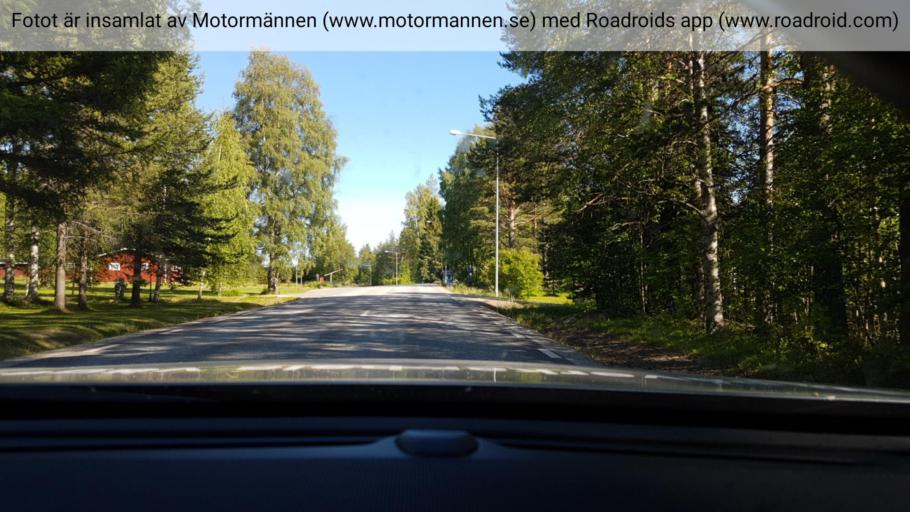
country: SE
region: Vaesterbotten
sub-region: Lycksele Kommun
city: Lycksele
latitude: 64.6360
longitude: 18.5373
